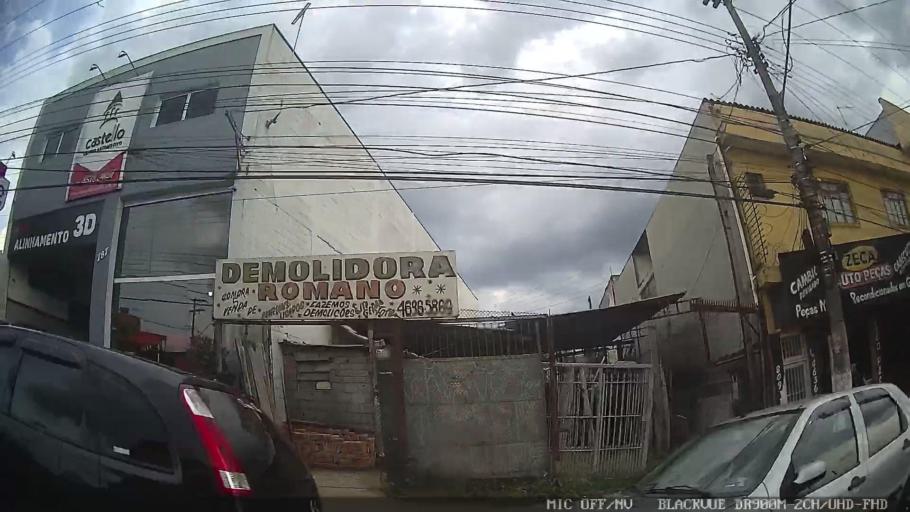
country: BR
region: Sao Paulo
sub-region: Poa
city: Poa
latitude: -23.5350
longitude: -46.3535
